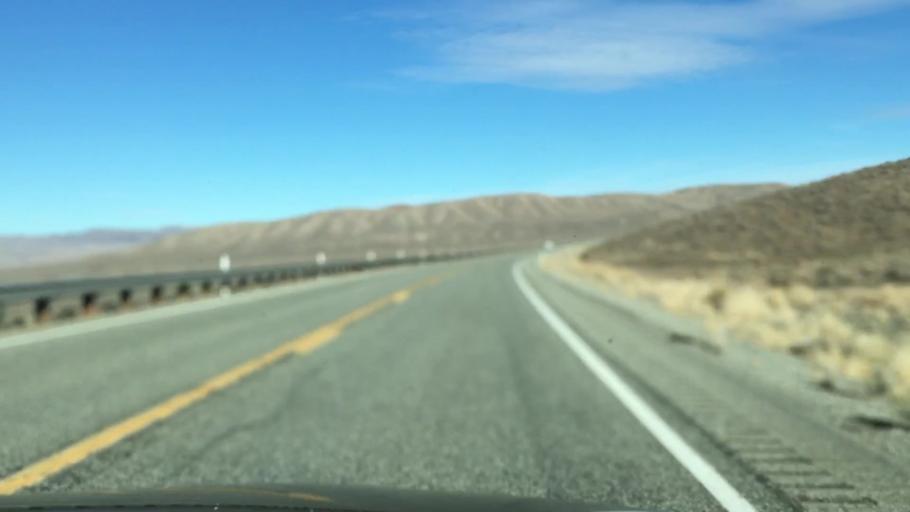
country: US
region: Nevada
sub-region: Lyon County
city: Yerington
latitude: 39.0435
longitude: -118.9813
